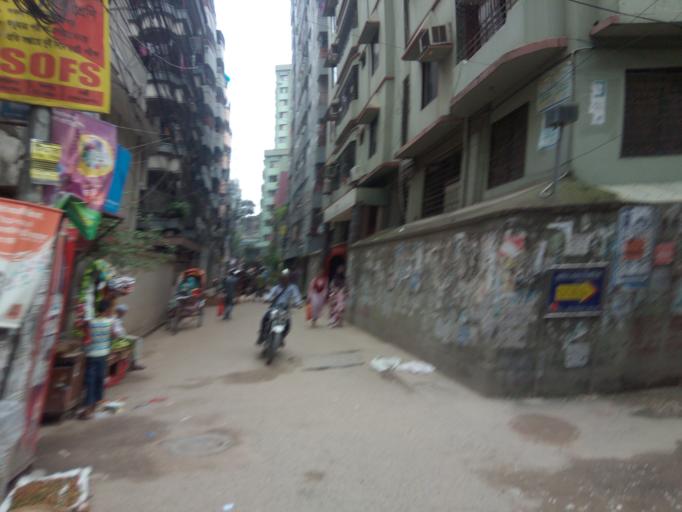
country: BD
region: Dhaka
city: Paltan
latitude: 23.7398
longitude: 90.4136
